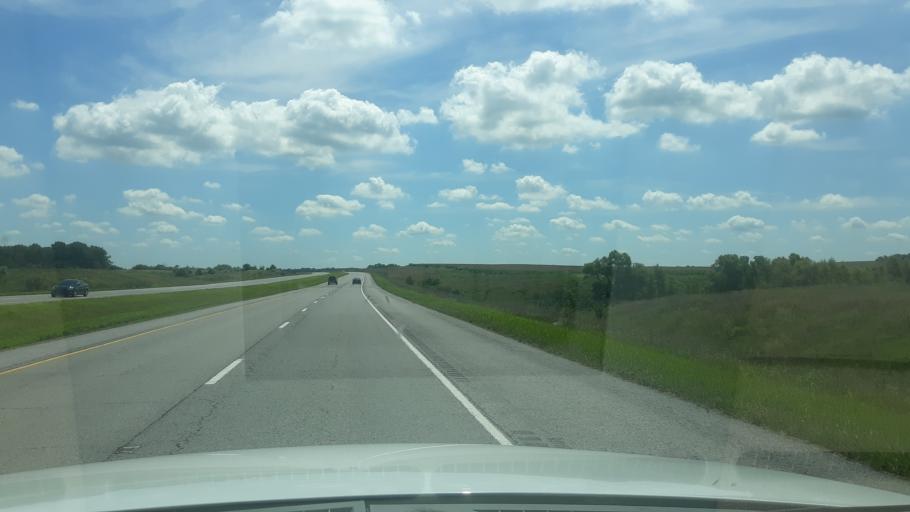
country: US
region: Illinois
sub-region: Saline County
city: Carrier Mills
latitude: 37.7316
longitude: -88.6091
